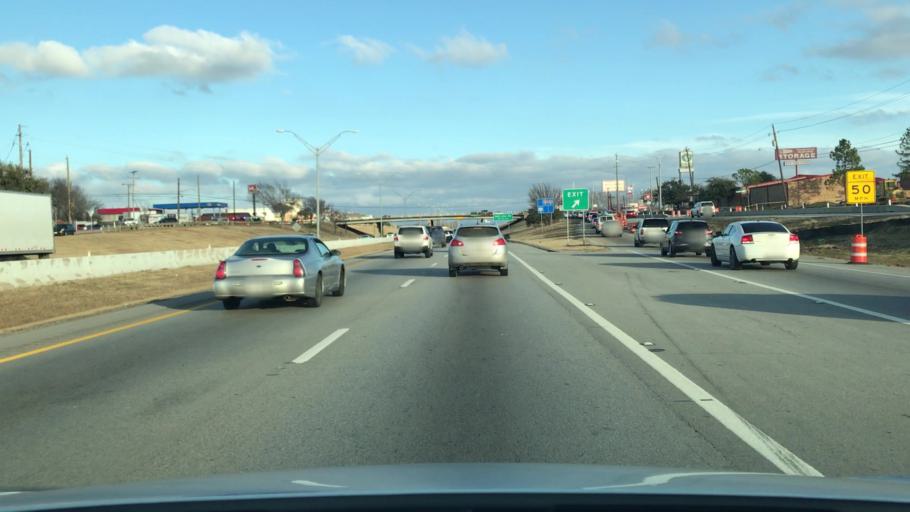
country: US
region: Texas
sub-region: Dallas County
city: Mesquite
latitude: 32.7925
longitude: -96.6151
